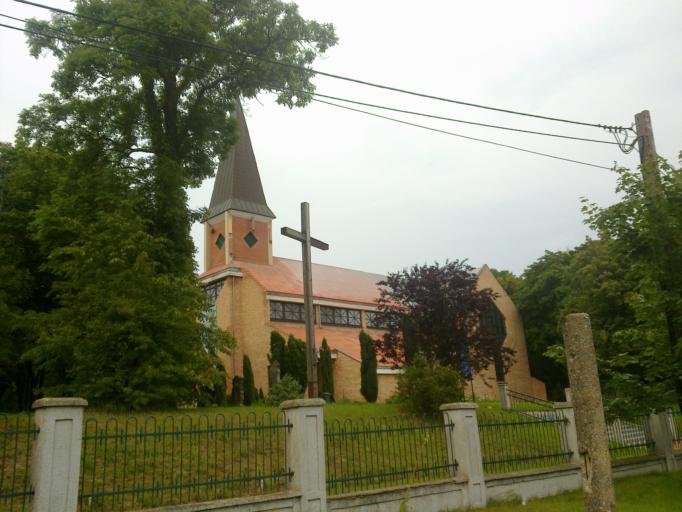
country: PL
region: Pomeranian Voivodeship
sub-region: Powiat gdanski
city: Cedry Wielkie
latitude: 54.3439
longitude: 18.8257
